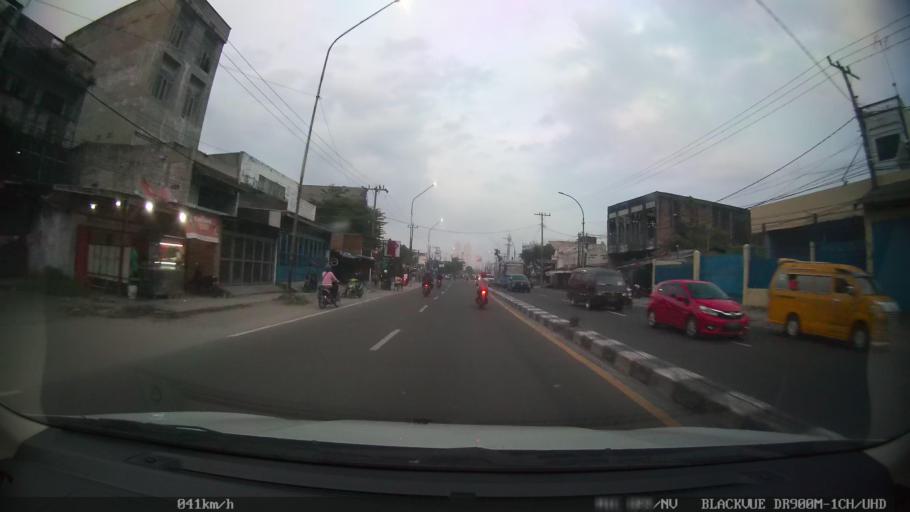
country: ID
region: North Sumatra
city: Sunggal
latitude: 3.5975
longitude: 98.6102
